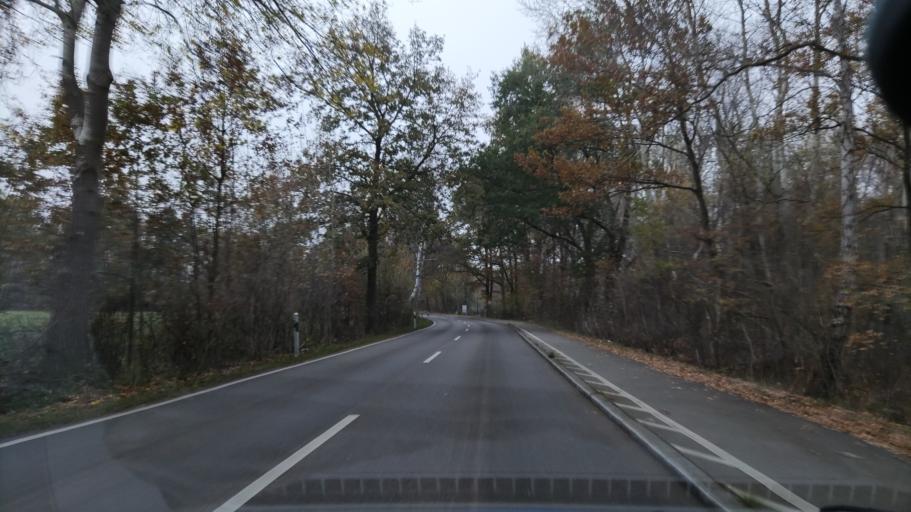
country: DE
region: Schleswig-Holstein
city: Gross Gronau
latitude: 53.8132
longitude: 10.7113
